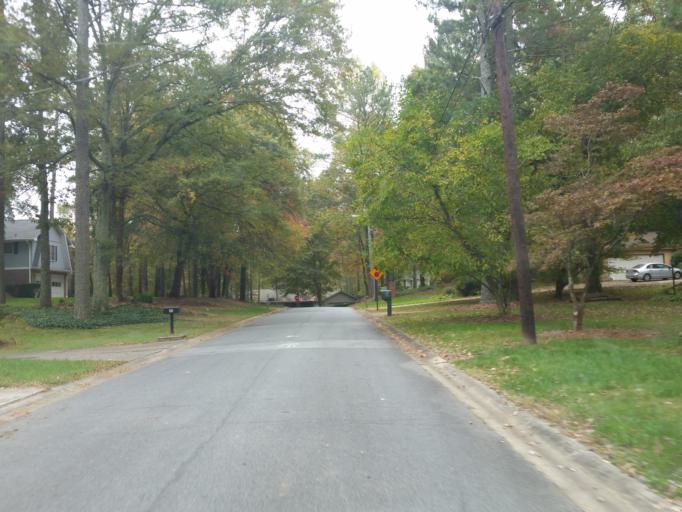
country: US
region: Georgia
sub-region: Cobb County
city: Marietta
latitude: 33.9507
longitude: -84.4714
